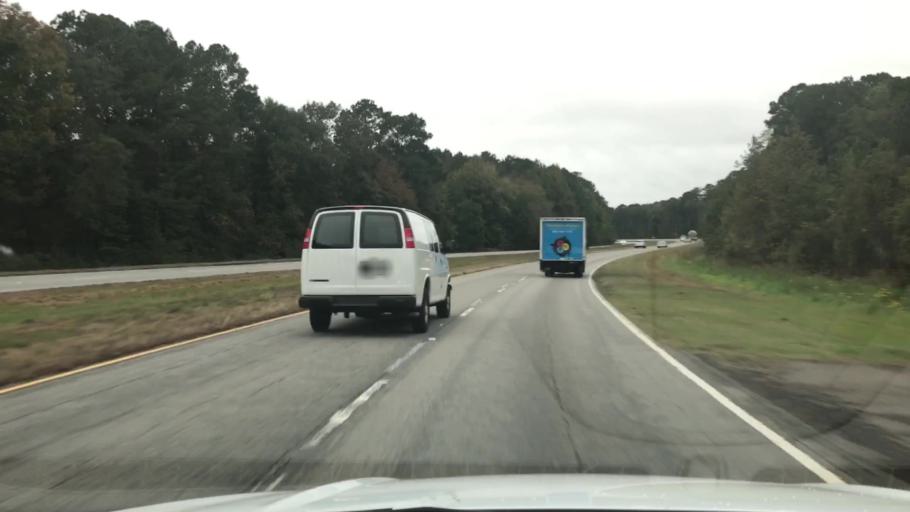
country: US
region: South Carolina
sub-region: Charleston County
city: Ravenel
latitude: 32.7583
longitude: -80.3828
